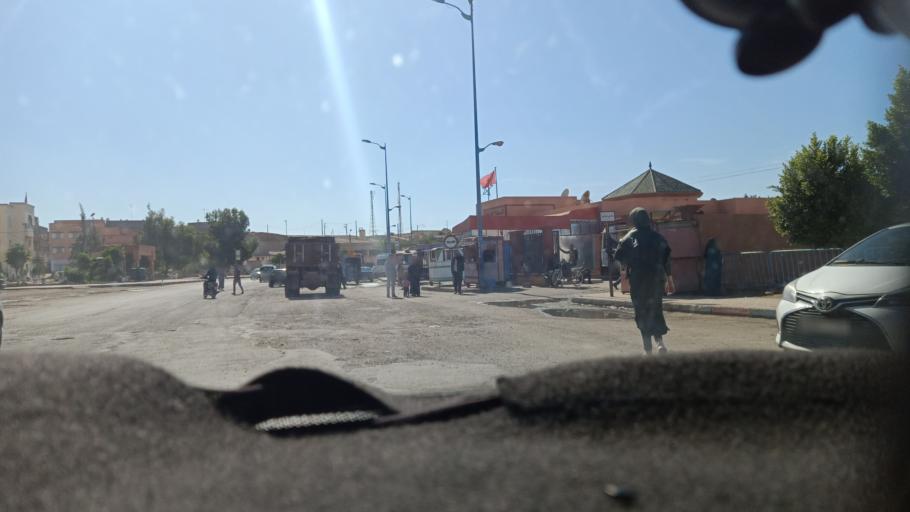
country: MA
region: Doukkala-Abda
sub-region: Safi
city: Youssoufia
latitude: 32.2398
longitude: -8.5392
